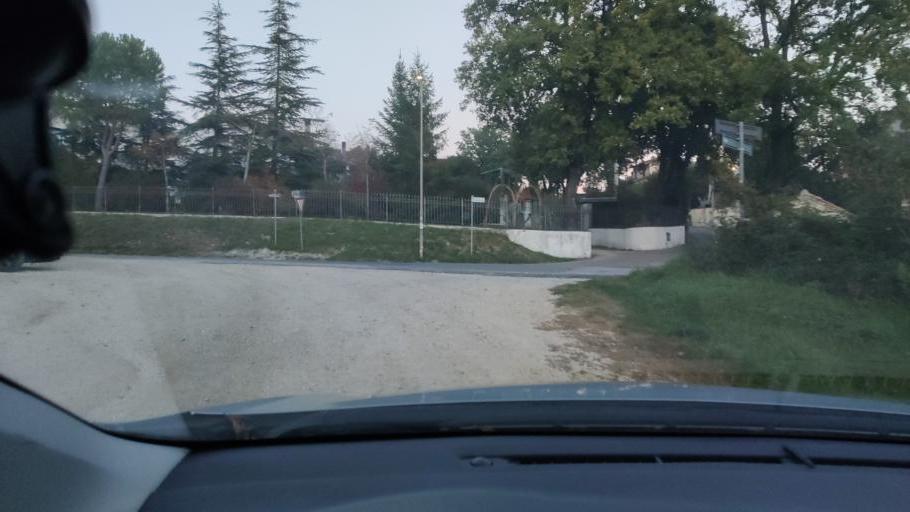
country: IT
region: Umbria
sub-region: Provincia di Terni
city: Amelia
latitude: 42.5969
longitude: 12.4368
